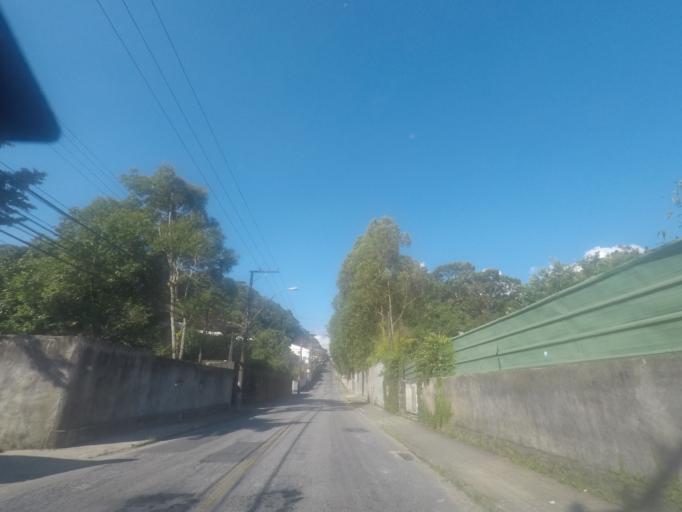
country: BR
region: Rio de Janeiro
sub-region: Petropolis
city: Petropolis
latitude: -22.5326
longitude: -43.1943
